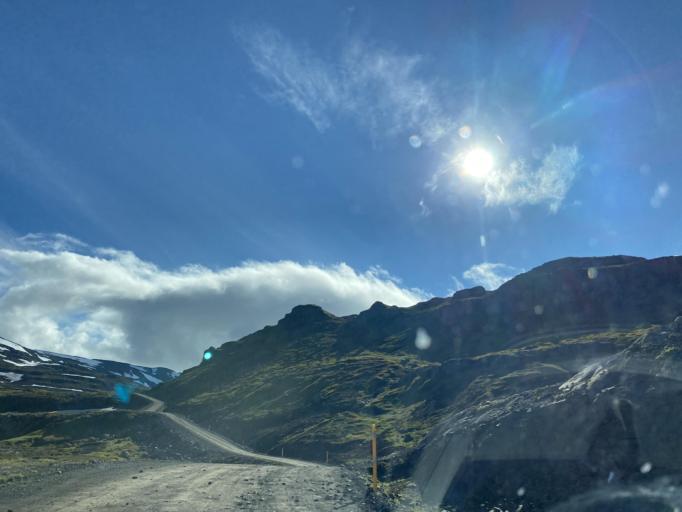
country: IS
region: East
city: Eskifjoerdur
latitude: 65.1768
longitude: -14.1104
